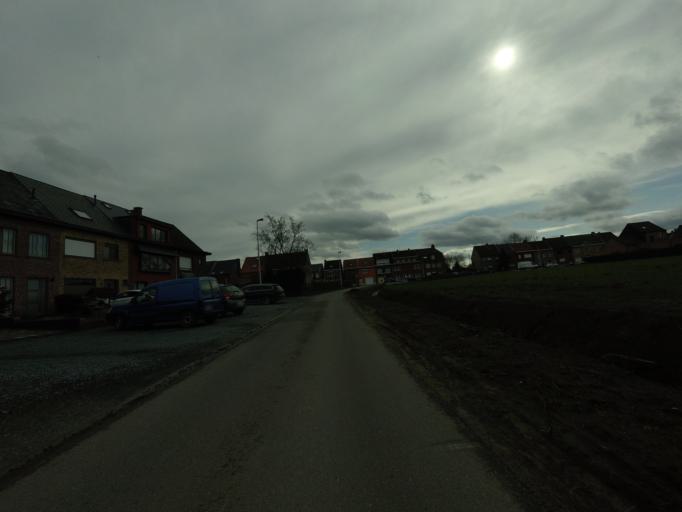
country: BE
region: Flanders
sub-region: Provincie Antwerpen
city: Schelle
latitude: 51.1266
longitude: 4.3566
